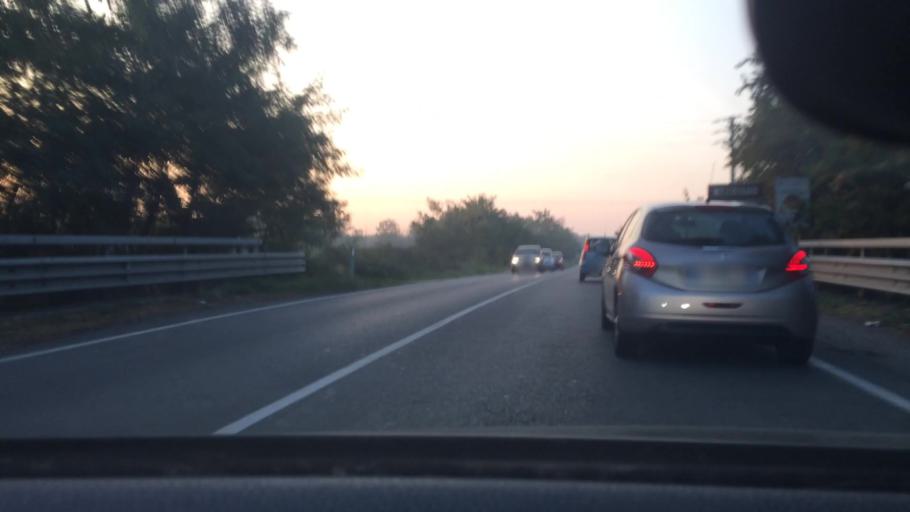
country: IT
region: Lombardy
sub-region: Citta metropolitana di Milano
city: Parabiago
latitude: 45.5396
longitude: 8.9612
